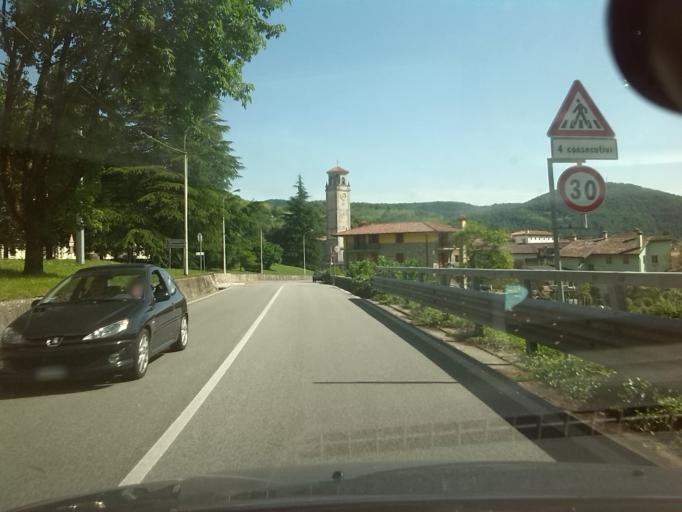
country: IT
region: Friuli Venezia Giulia
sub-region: Provincia di Udine
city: San Pietro al Natisone
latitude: 46.1310
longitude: 13.4857
